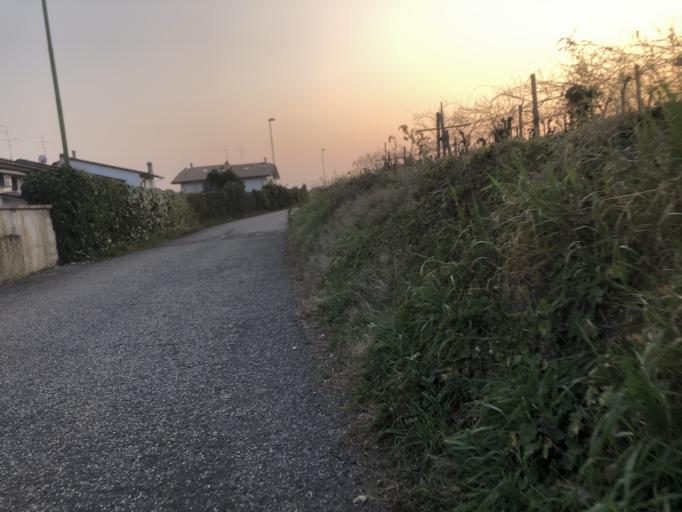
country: IT
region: Veneto
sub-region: Provincia di Verona
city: Sommacampagna
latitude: 45.4016
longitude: 10.8353
